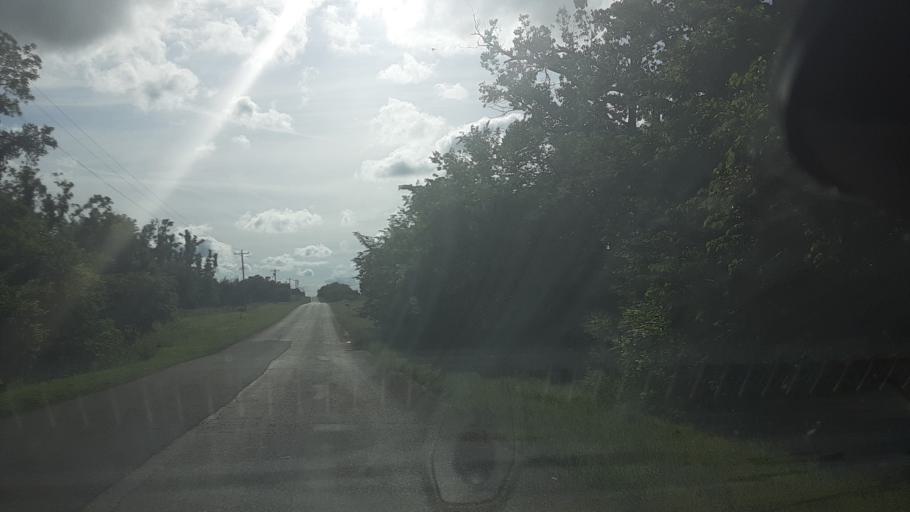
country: US
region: Oklahoma
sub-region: Logan County
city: Langston
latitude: 36.0579
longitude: -97.3682
